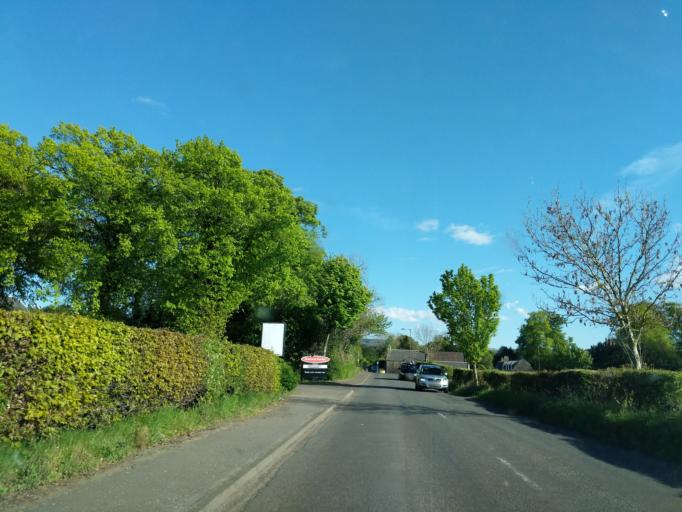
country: GB
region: Scotland
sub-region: Edinburgh
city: Ratho
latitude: 55.9093
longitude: -3.3700
